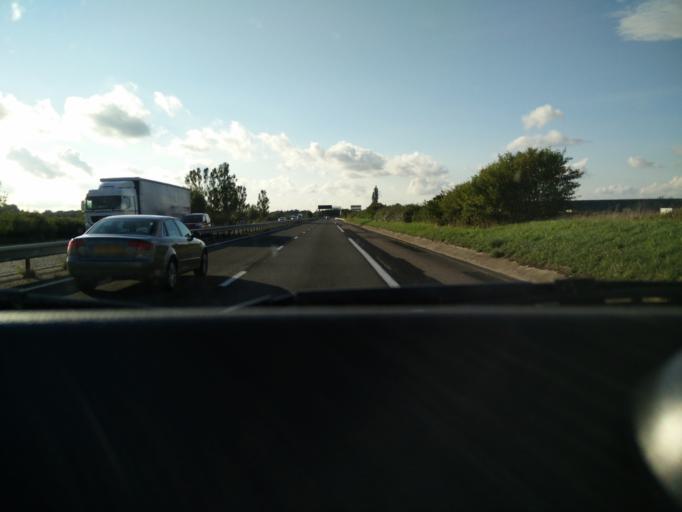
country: FR
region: Lorraine
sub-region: Departement de Meurthe-et-Moselle
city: Chanteheux
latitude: 48.5442
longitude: 6.5677
